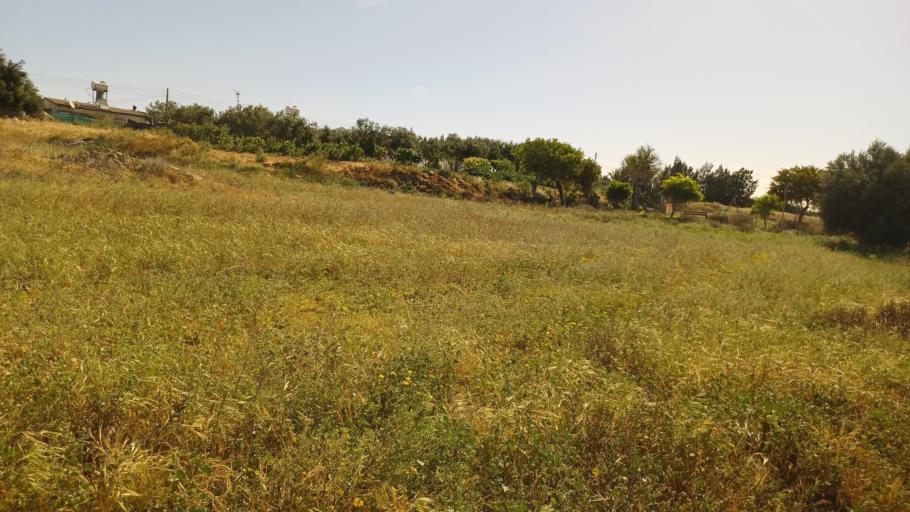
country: CY
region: Lefkosia
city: Kokkinotrimithia
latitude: 35.1540
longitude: 33.1858
